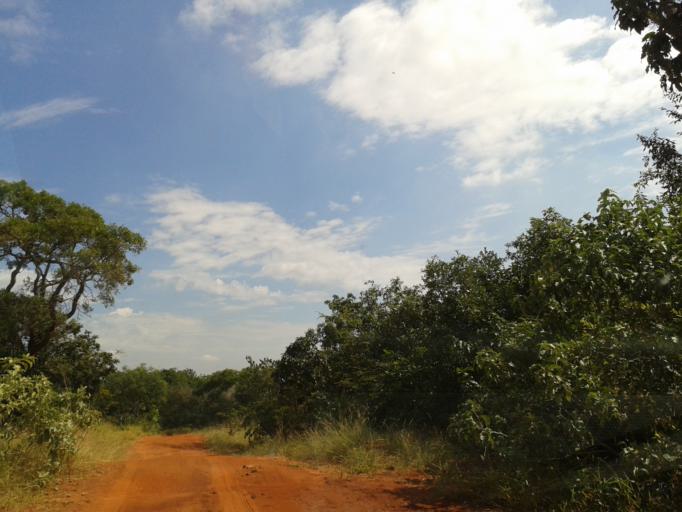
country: BR
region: Minas Gerais
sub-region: Campina Verde
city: Campina Verde
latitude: -19.3904
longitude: -49.6459
